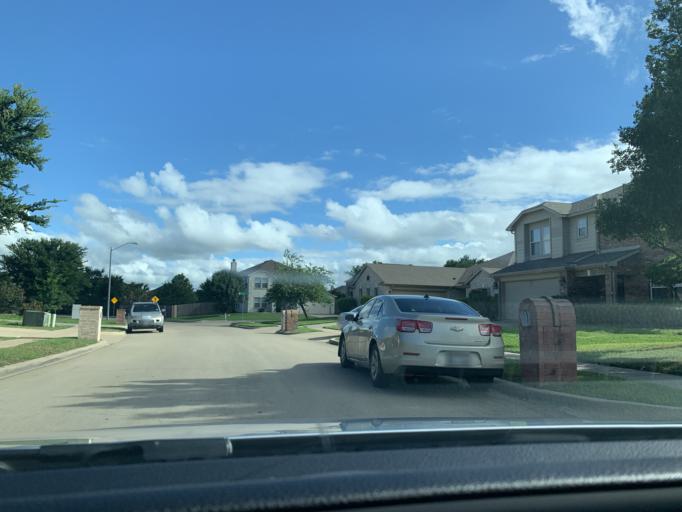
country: US
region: Texas
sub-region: Dallas County
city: Cedar Hill
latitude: 32.6440
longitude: -97.0369
